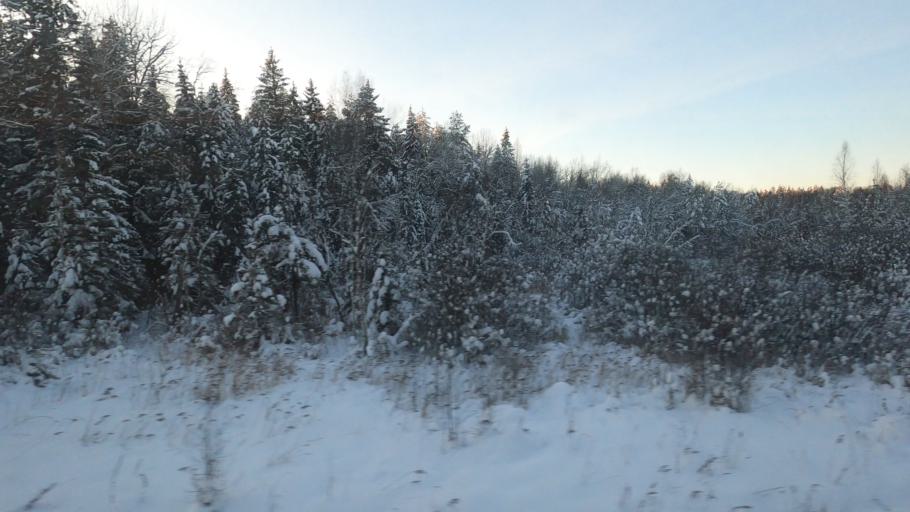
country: RU
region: Moskovskaya
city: Verbilki
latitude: 56.5252
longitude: 37.5583
